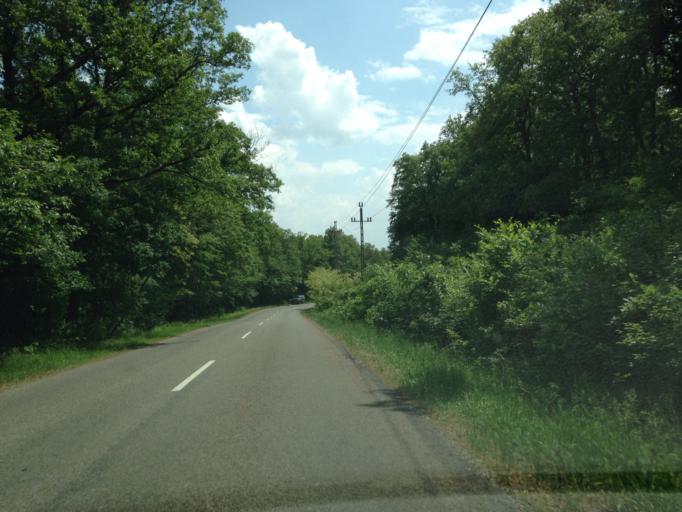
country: HU
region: Pest
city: Nagykovacsi
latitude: 47.7113
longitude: 19.0149
